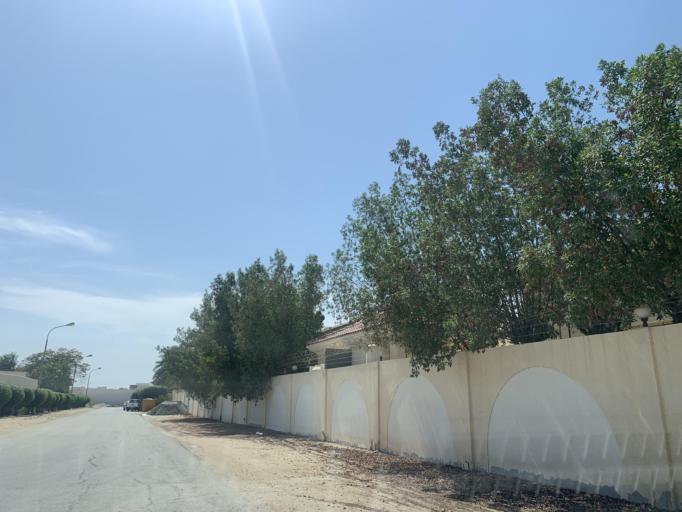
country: BH
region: Central Governorate
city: Madinat Hamad
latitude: 26.1783
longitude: 50.4713
